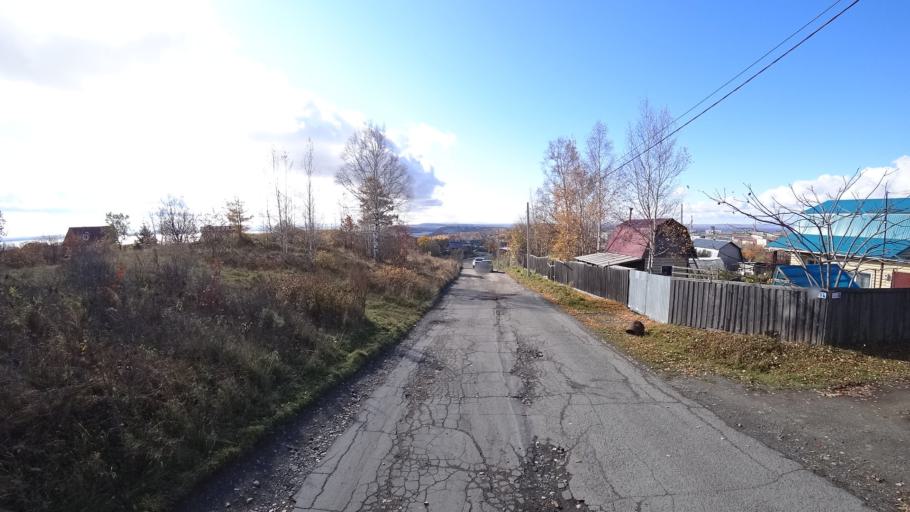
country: RU
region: Khabarovsk Krai
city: Amursk
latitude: 50.2371
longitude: 136.9243
